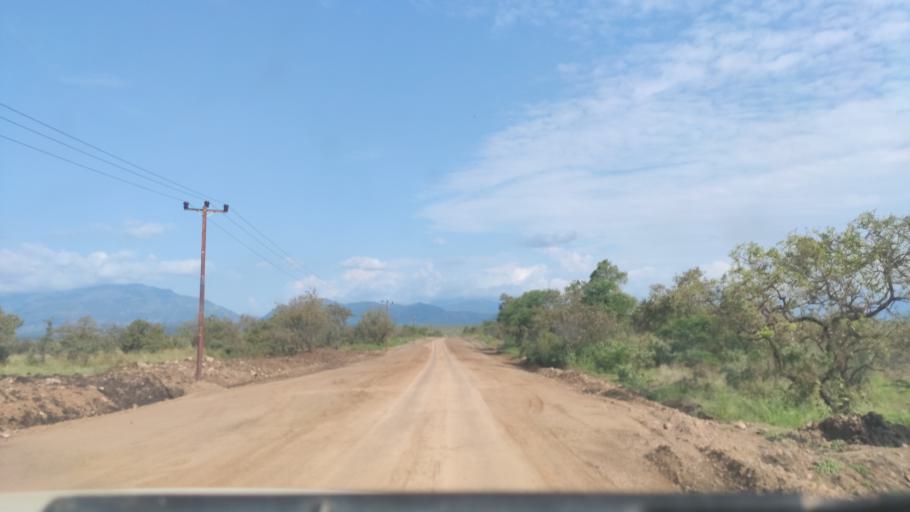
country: ET
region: Southern Nations, Nationalities, and People's Region
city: Felege Neway
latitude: 6.4265
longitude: 37.2282
